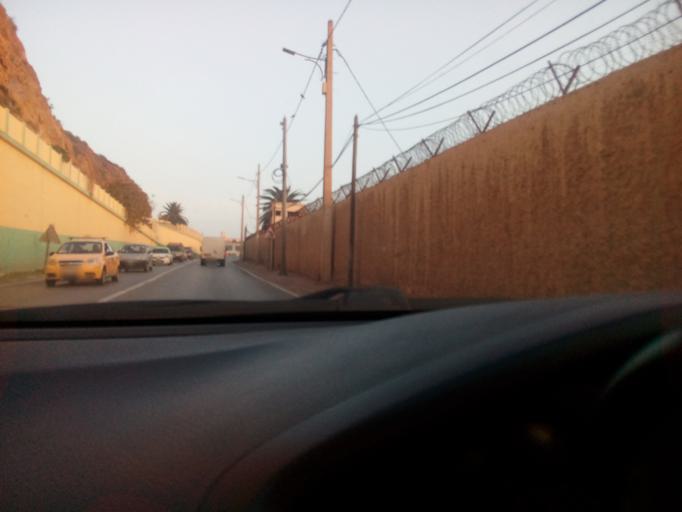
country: DZ
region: Oran
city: Oran
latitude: 35.7118
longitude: -0.6569
